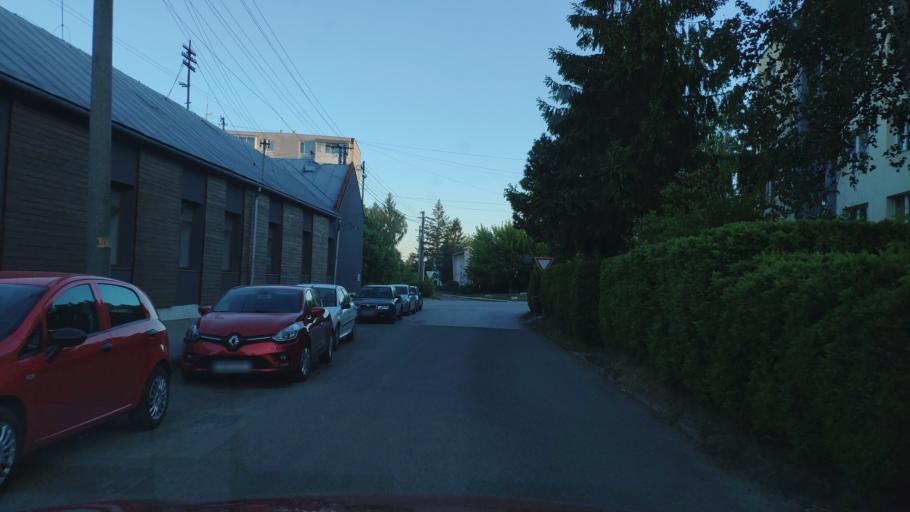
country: SK
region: Kosicky
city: Secovce
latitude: 48.7028
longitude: 21.6589
